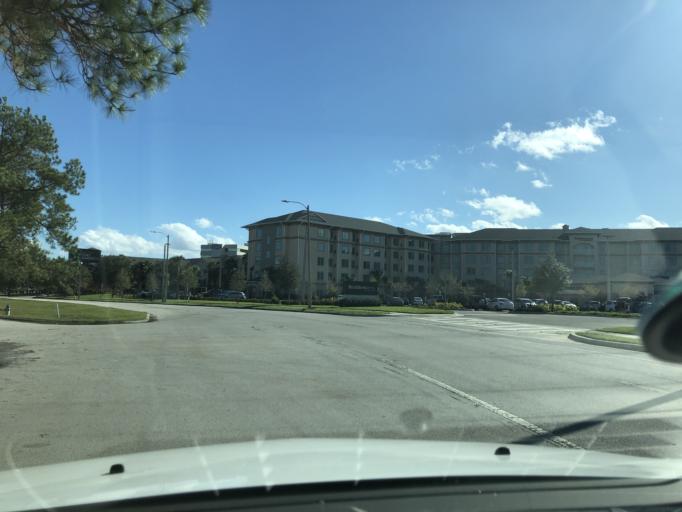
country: US
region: Florida
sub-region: Orange County
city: Tangelo Park
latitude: 28.4817
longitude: -81.4553
